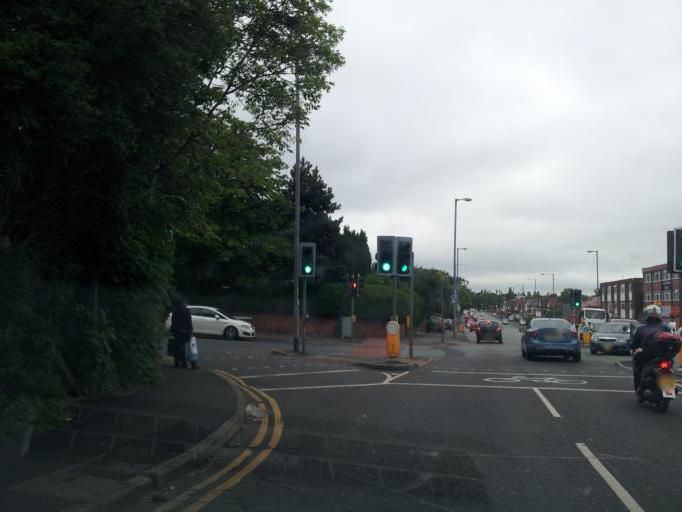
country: GB
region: England
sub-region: Manchester
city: Crumpsall
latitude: 53.5256
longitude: -2.2483
